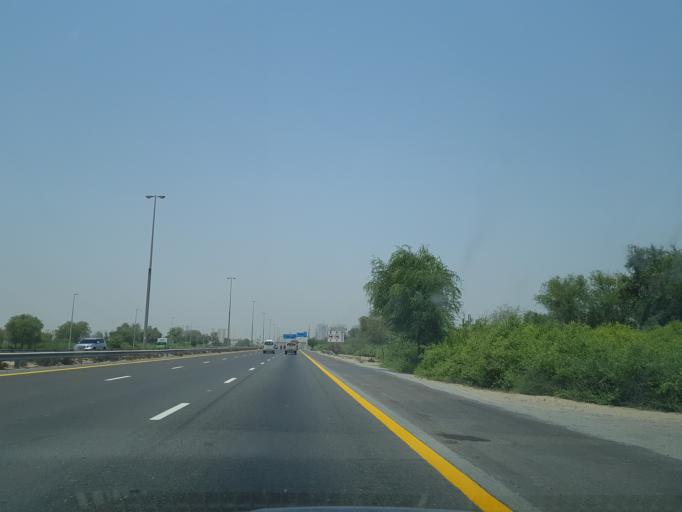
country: AE
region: Dubai
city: Dubai
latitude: 25.0965
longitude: 55.3848
